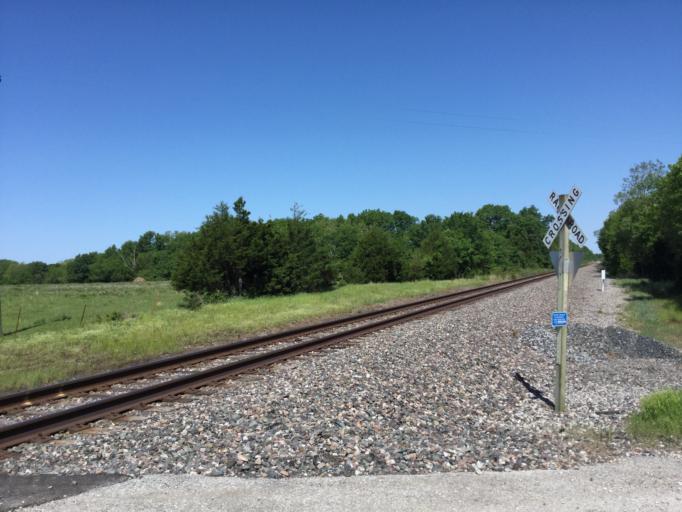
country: US
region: Kansas
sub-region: Labette County
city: Parsons
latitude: 37.2672
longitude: -95.2223
